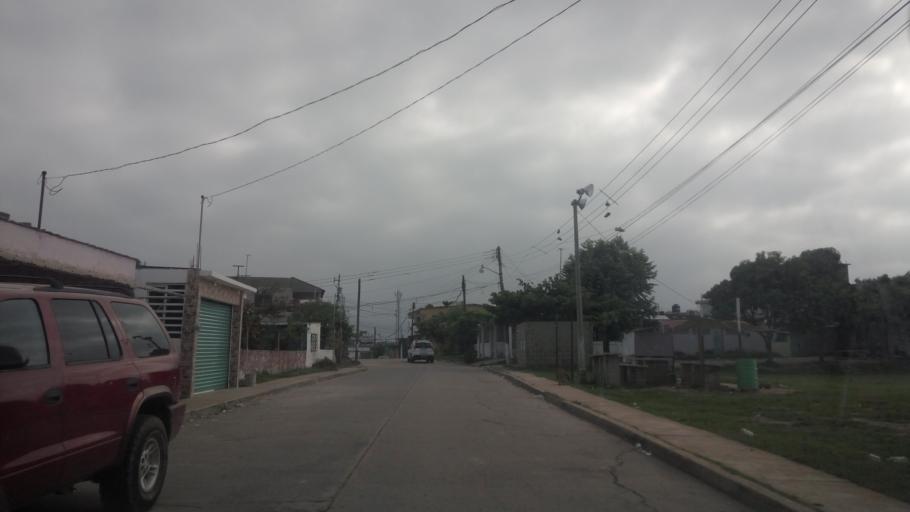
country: MX
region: Chiapas
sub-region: Reforma
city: El Carmen (El Limon)
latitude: 17.8592
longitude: -93.1518
